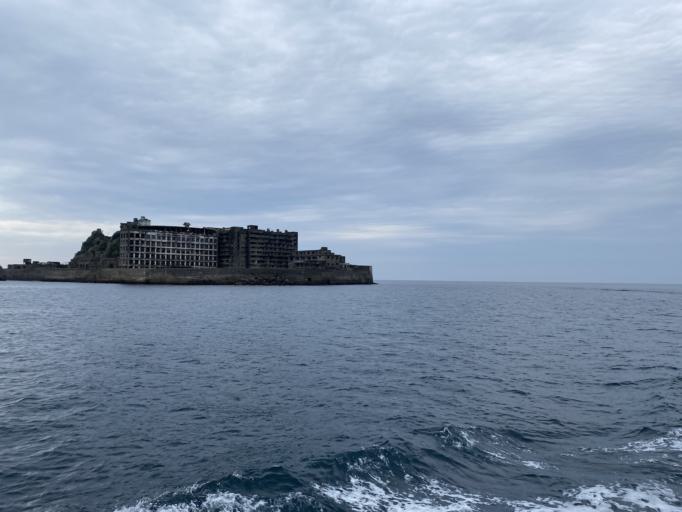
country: JP
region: Nagasaki
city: Nagasaki-shi
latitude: 32.6302
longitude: 129.7422
